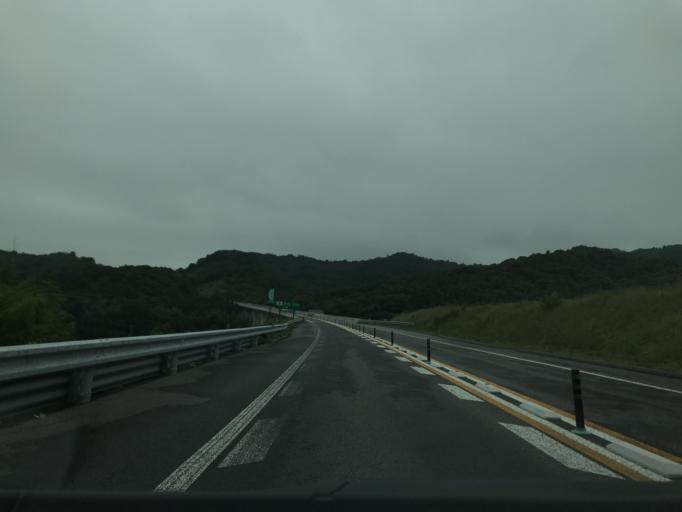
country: JP
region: Fukuoka
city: Nakatsu
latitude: 33.5053
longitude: 131.2967
